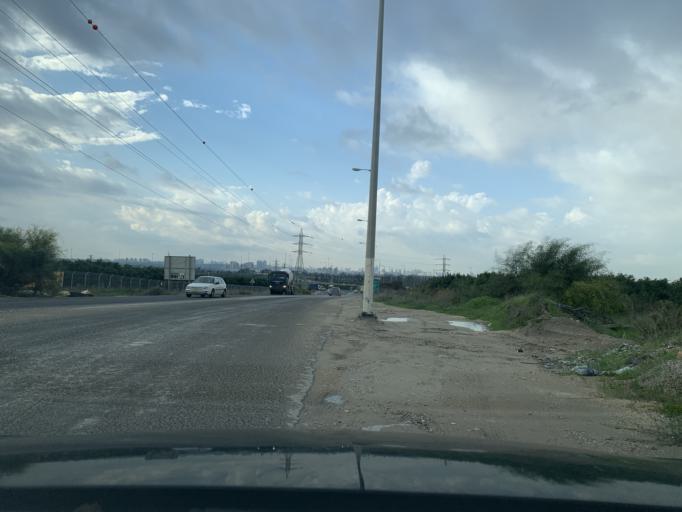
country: IL
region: Central District
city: Rosh Ha'Ayin
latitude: 32.0669
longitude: 34.9471
